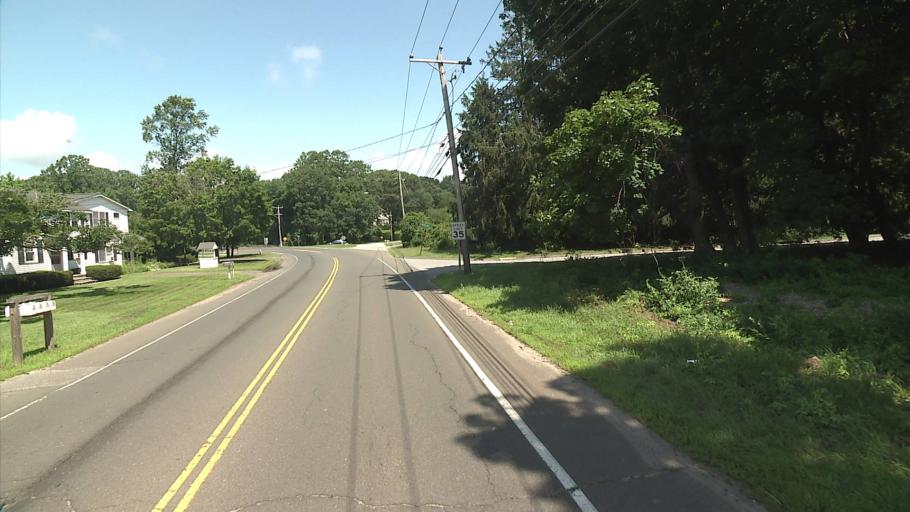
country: US
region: Connecticut
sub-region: Middlesex County
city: Saybrook Manor
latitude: 41.2925
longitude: -72.4208
